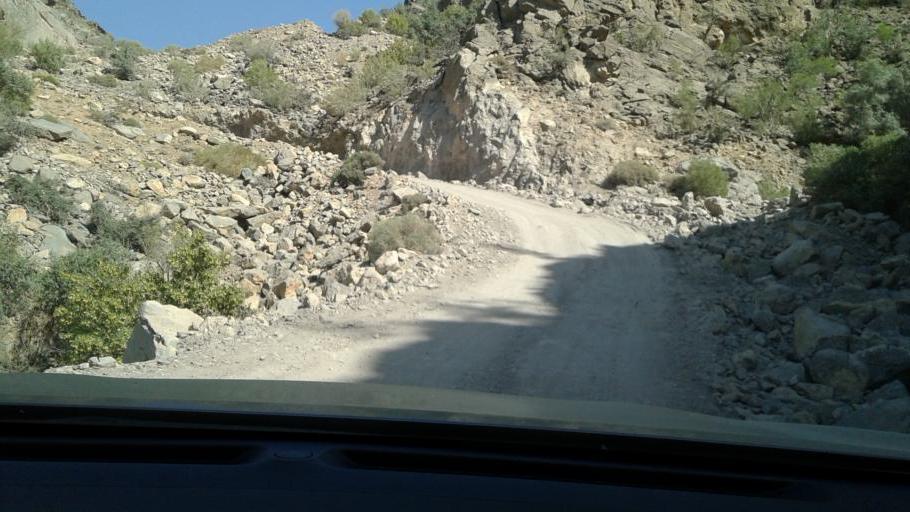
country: OM
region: Al Batinah
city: Bayt al `Awabi
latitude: 23.1765
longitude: 57.4118
